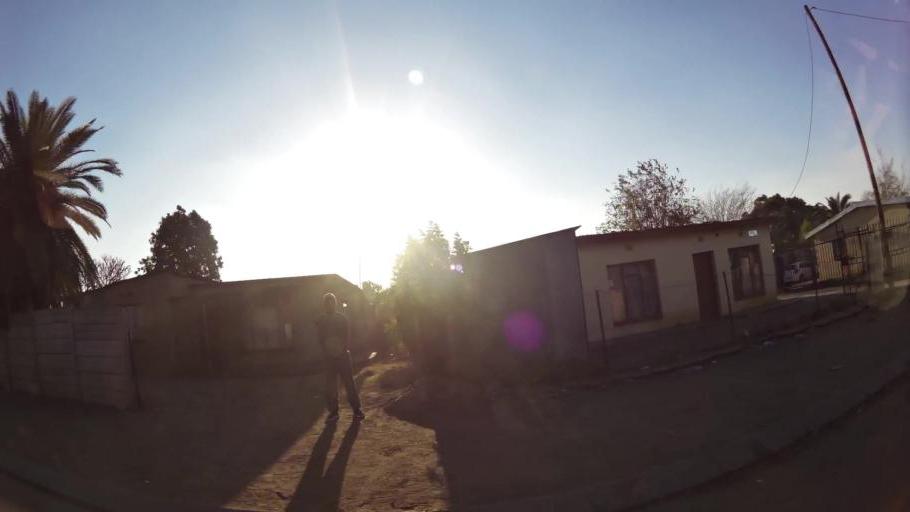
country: ZA
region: North-West
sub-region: Bojanala Platinum District Municipality
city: Rustenburg
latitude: -25.6374
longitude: 27.2209
